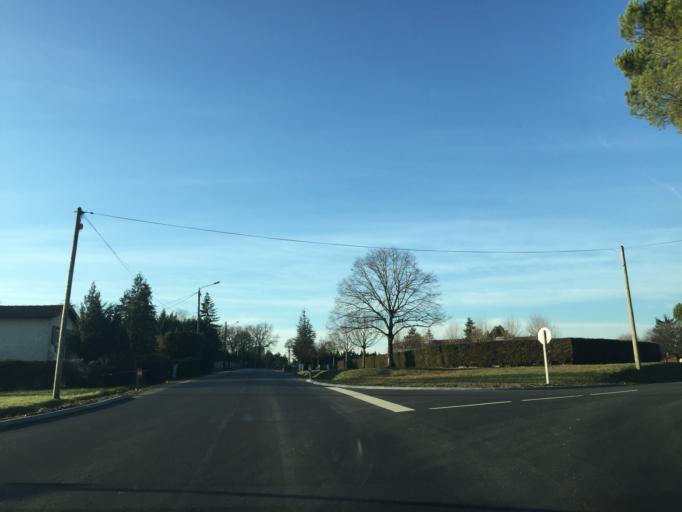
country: FR
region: Aquitaine
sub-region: Departement de la Dordogne
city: Saint-Aulaye
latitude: 45.2741
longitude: 0.1497
